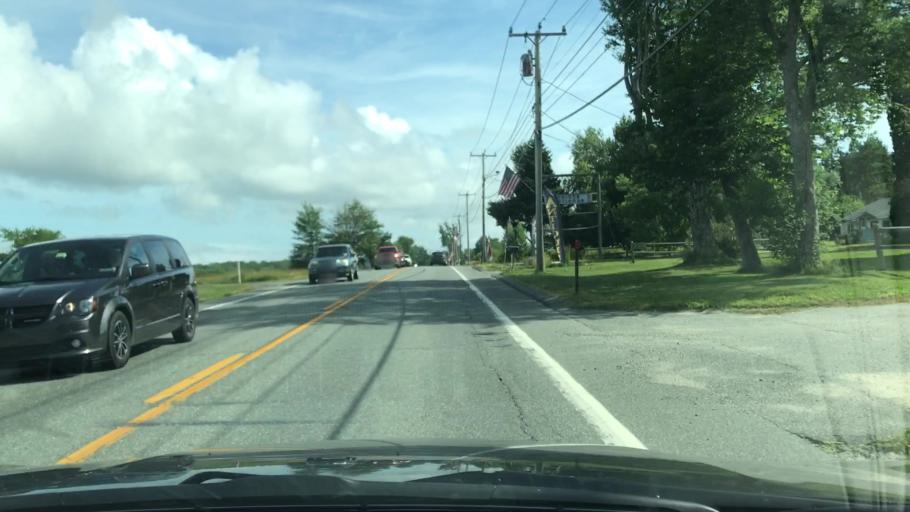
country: US
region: Maine
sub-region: Hancock County
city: Trenton
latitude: 44.4635
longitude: -68.3618
